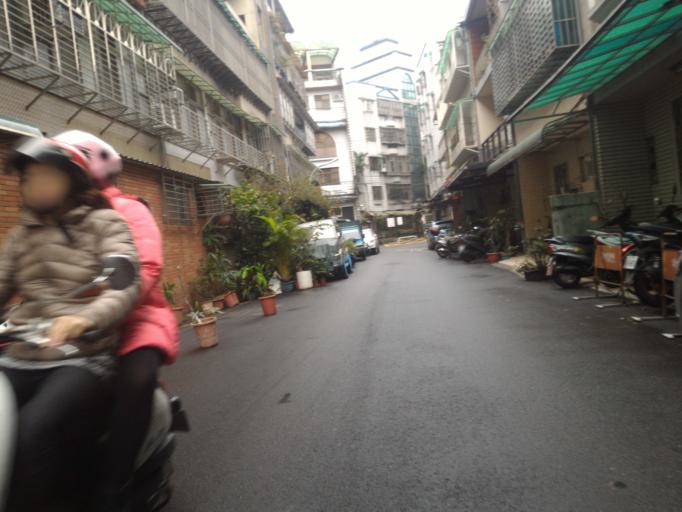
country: TW
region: Taipei
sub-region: Taipei
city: Banqiao
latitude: 25.0389
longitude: 121.4575
